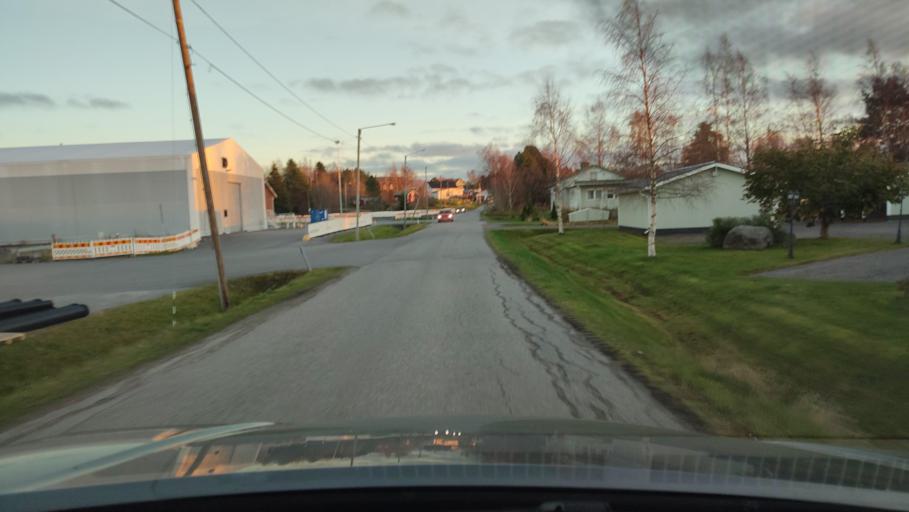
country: FI
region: Ostrobothnia
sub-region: Sydosterbotten
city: Kristinestad
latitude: 62.3021
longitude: 21.4545
